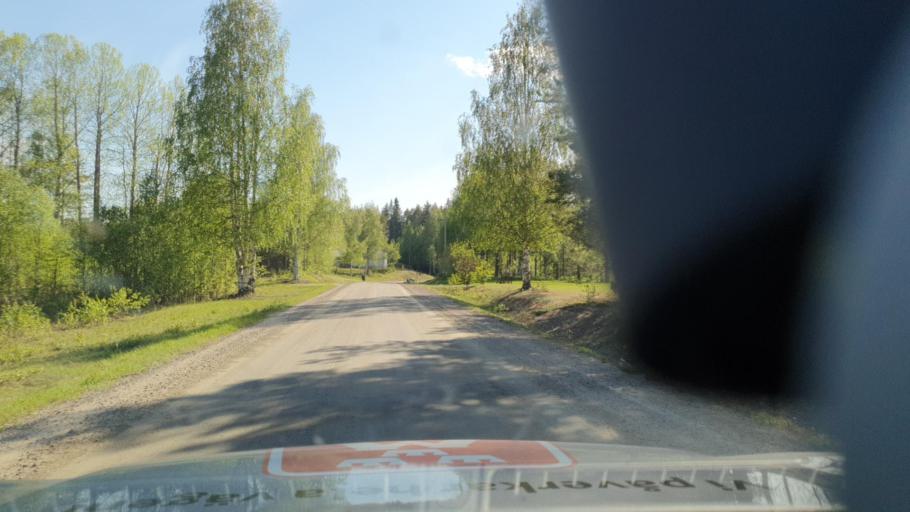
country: SE
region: Norrbotten
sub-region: Alvsbyns Kommun
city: AElvsbyn
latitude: 66.2652
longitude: 21.0819
